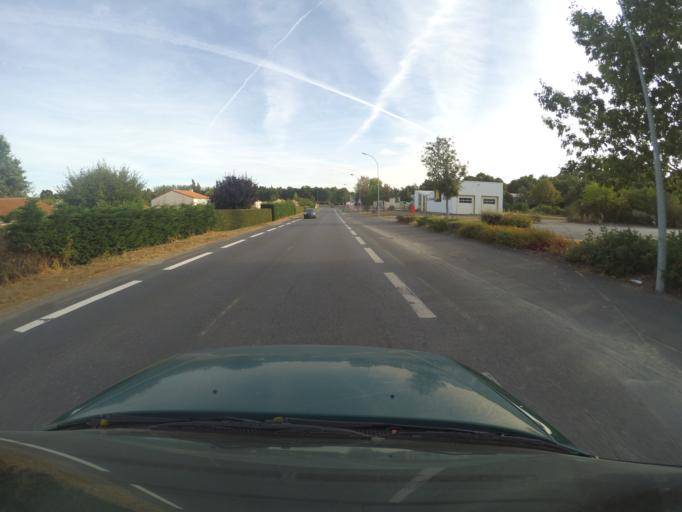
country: FR
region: Pays de la Loire
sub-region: Departement de la Vendee
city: Bouffere
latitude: 46.9782
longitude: -1.3298
